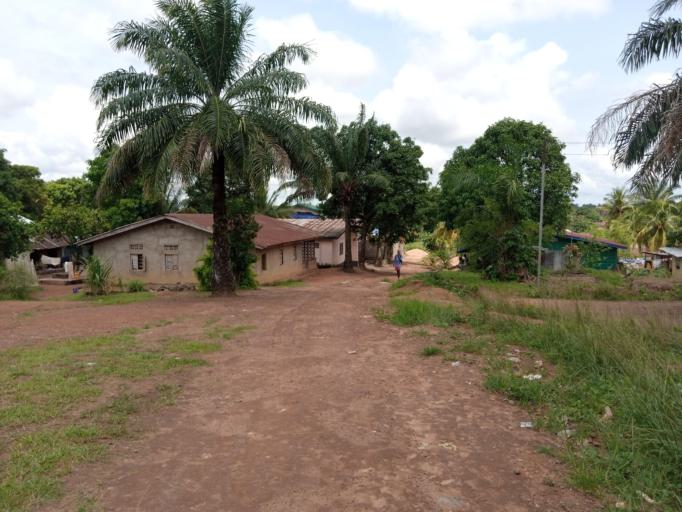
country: SL
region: Southern Province
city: Bo
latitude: 7.9451
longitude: -11.7215
